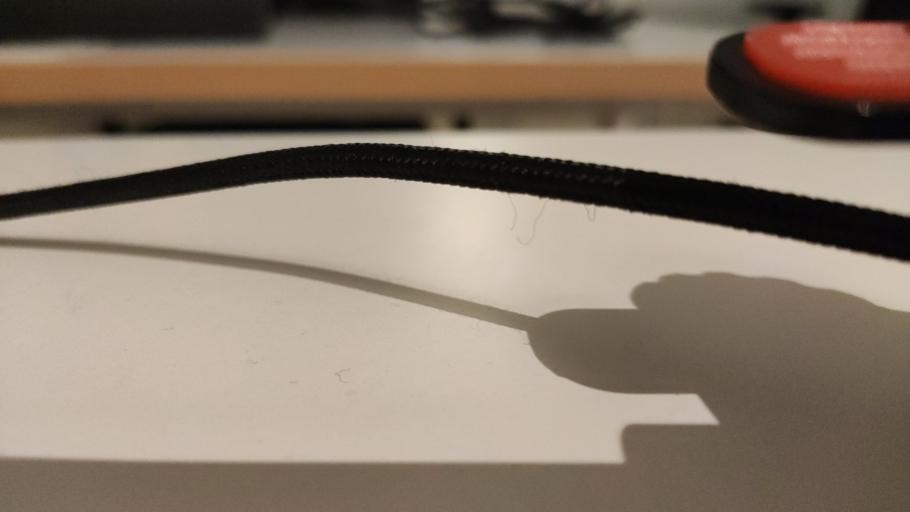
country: RU
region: Moskovskaya
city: Novosin'kovo
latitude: 56.3805
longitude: 37.3242
